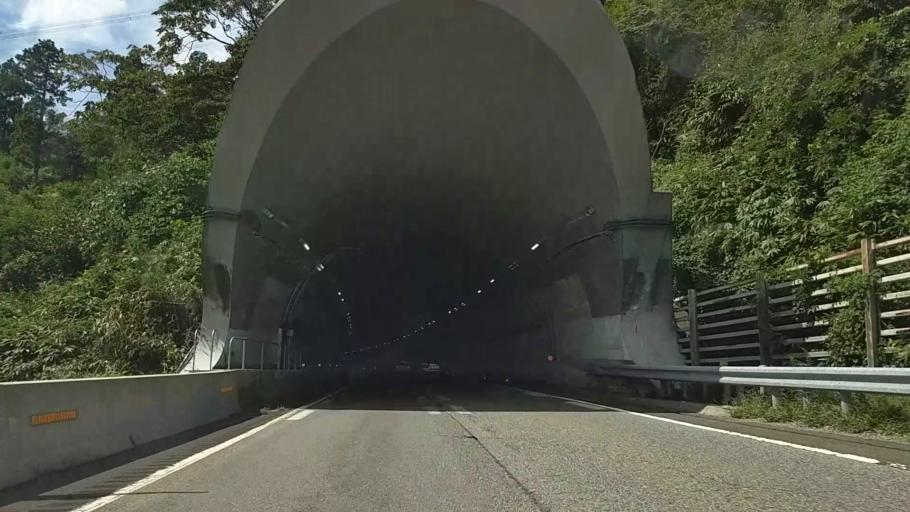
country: JP
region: Ishikawa
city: Tsubata
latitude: 36.6042
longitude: 136.7930
